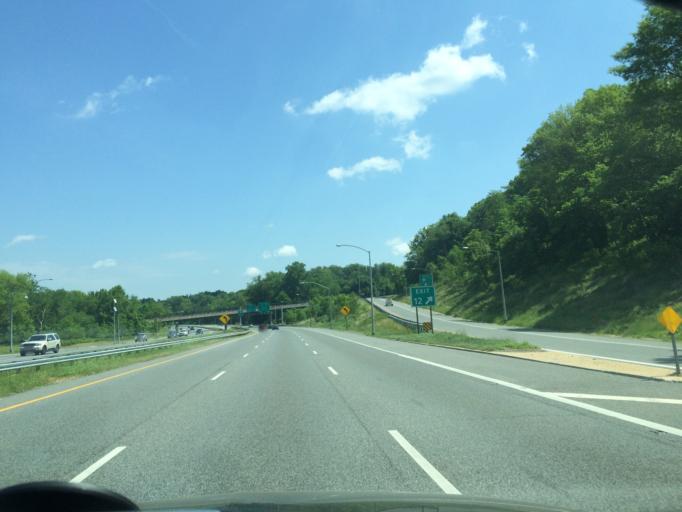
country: US
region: Maryland
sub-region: Baltimore County
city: Mays Chapel
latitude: 39.3985
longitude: -76.6645
